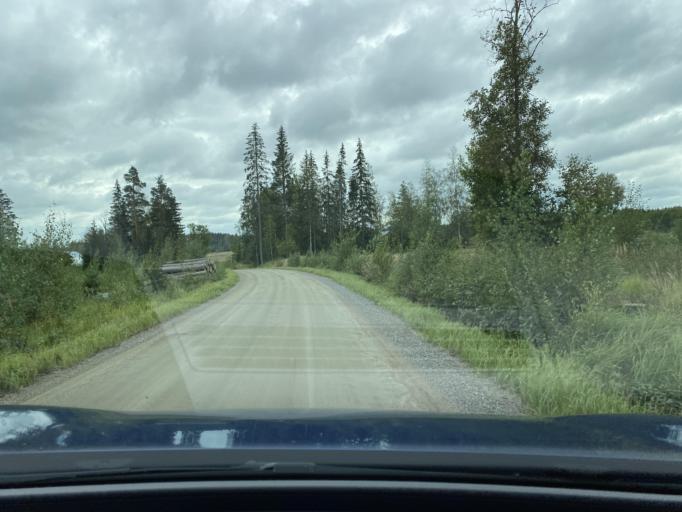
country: FI
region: Pirkanmaa
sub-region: Lounais-Pirkanmaa
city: Punkalaidun
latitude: 61.1885
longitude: 23.1834
